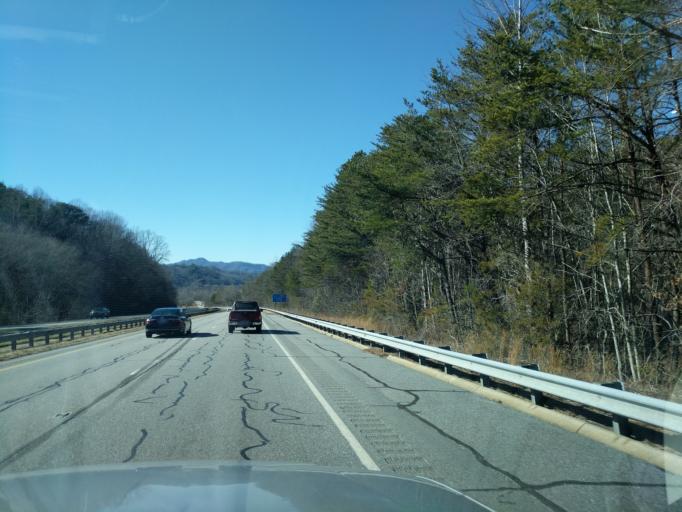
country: US
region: North Carolina
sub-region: Swain County
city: Bryson City
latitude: 35.4357
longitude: -83.3875
